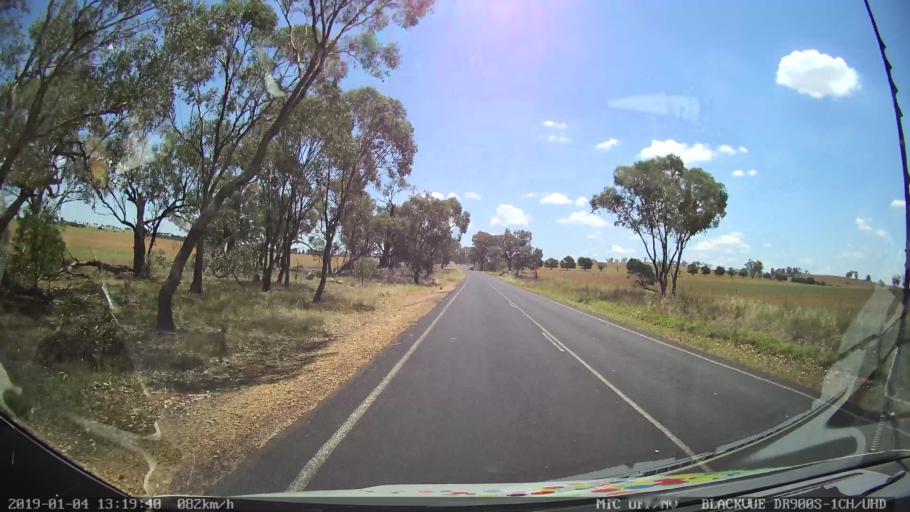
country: AU
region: New South Wales
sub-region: Wellington
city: Wellington
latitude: -32.7455
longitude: 148.6031
